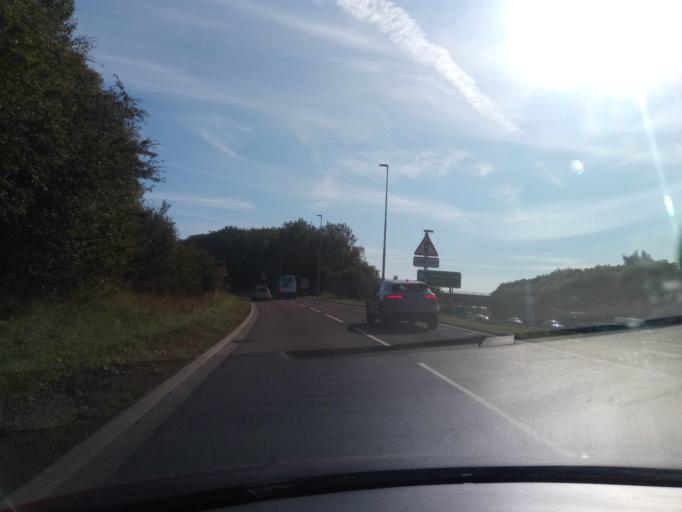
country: GB
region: England
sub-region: Sunderland
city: Washington
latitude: 54.9063
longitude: -1.5608
